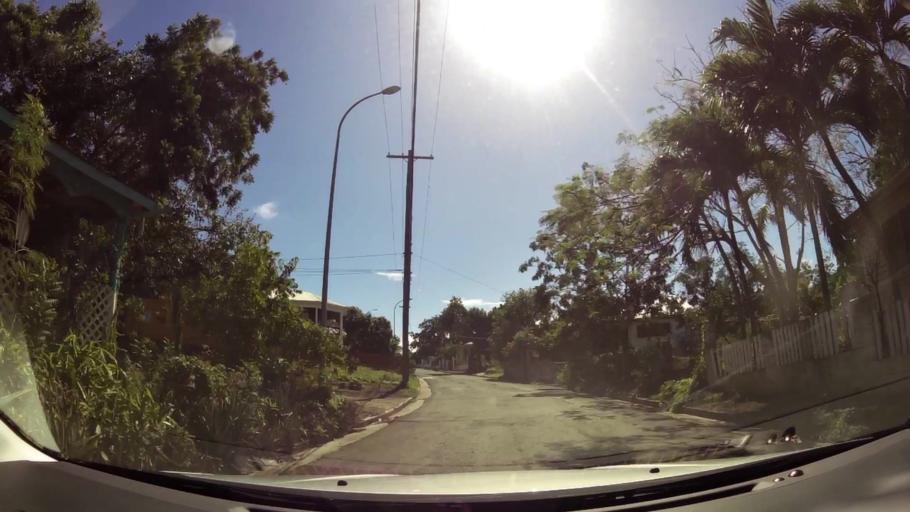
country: AG
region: Saint Paul
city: Falmouth
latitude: 17.0173
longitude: -61.7661
